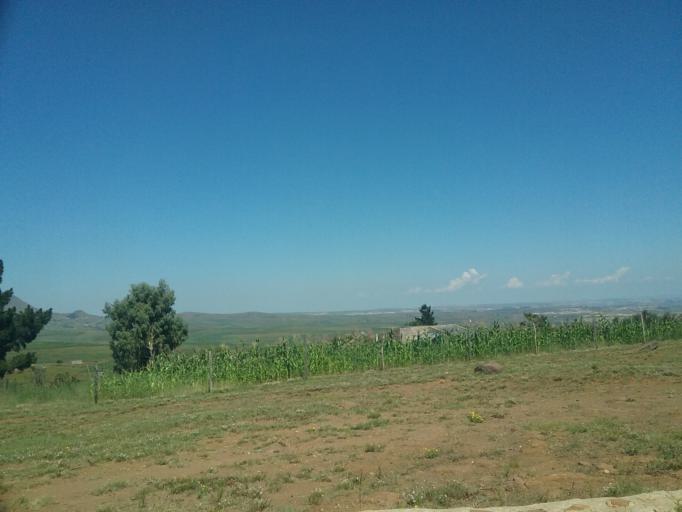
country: LS
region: Berea
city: Teyateyaneng
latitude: -29.2229
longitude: 27.8679
